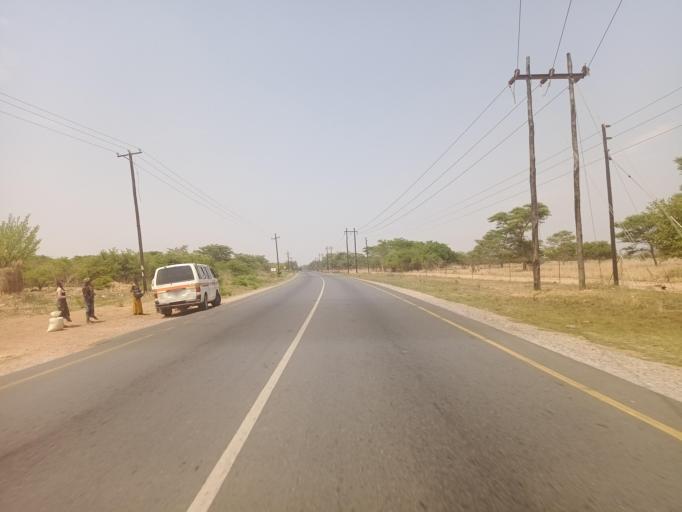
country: ZM
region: Lusaka
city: Lusaka
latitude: -15.2816
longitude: 28.3902
